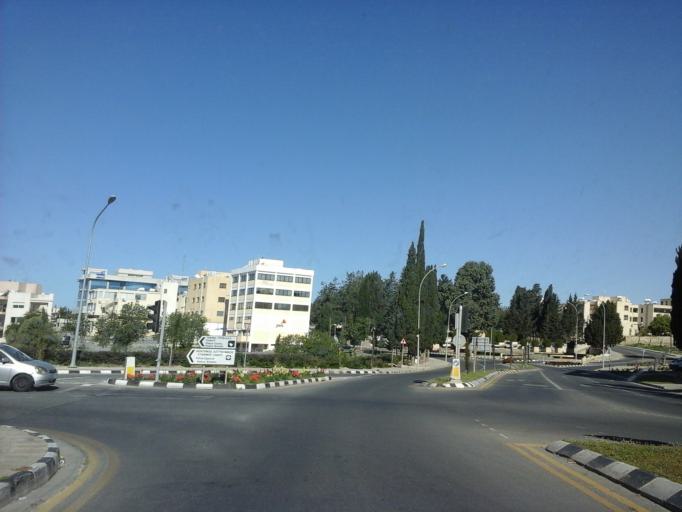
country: CY
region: Pafos
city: Paphos
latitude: 34.7706
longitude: 32.4331
